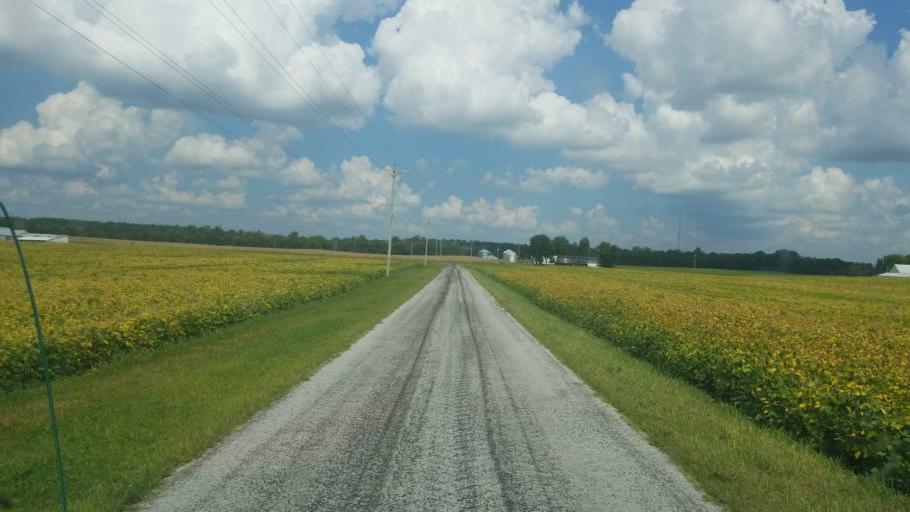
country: US
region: Ohio
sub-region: Hardin County
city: Kenton
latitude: 40.7008
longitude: -83.6386
